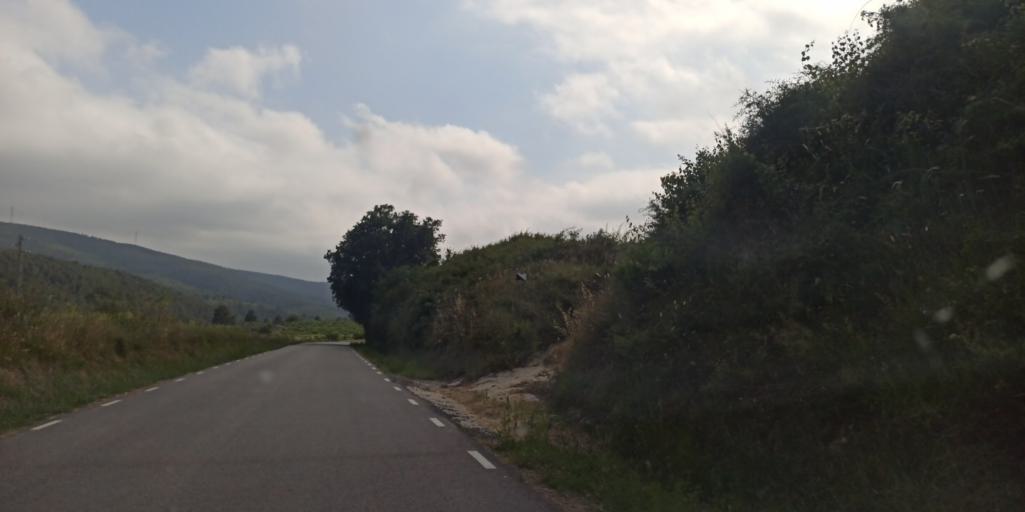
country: ES
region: Catalonia
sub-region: Provincia de Barcelona
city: Sant Joan de Mediona
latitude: 41.4719
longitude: 1.6003
